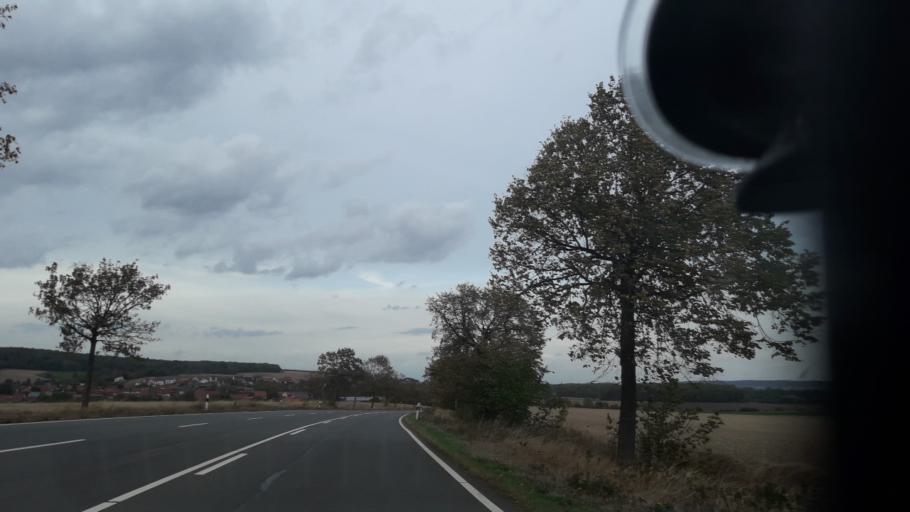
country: DE
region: Lower Saxony
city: Werlaburgdorf
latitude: 52.0422
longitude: 10.5401
